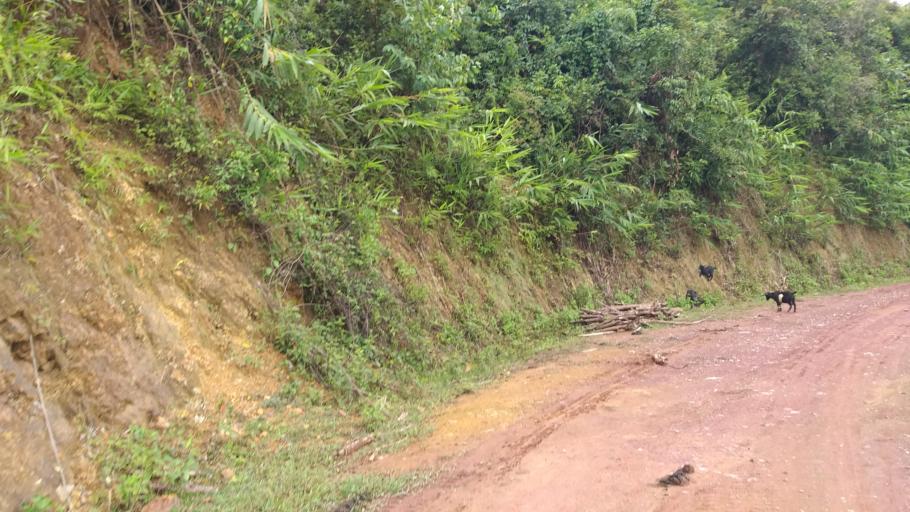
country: LA
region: Phongsali
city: Khoa
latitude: 21.3765
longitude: 102.6335
